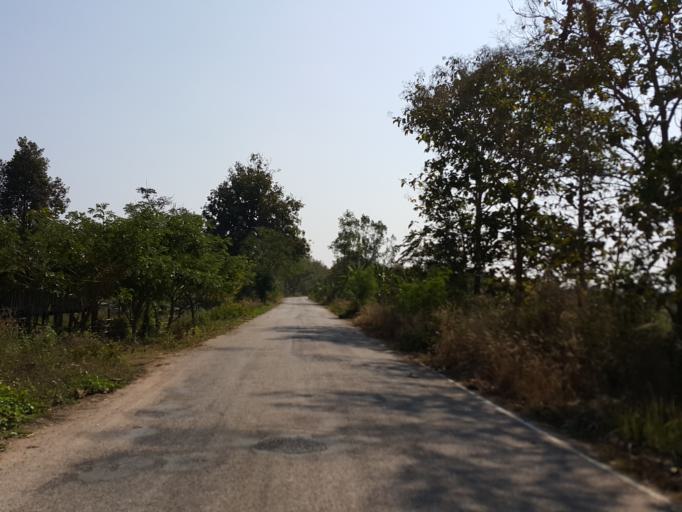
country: TH
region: Lampang
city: Wang Nuea
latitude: 19.0215
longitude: 99.6234
